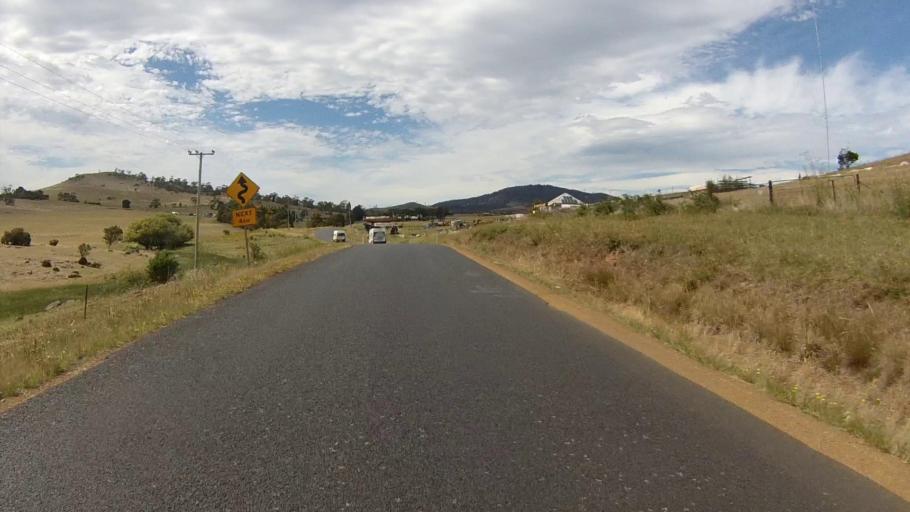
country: AU
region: Tasmania
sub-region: Brighton
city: Old Beach
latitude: -42.7024
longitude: 147.3094
